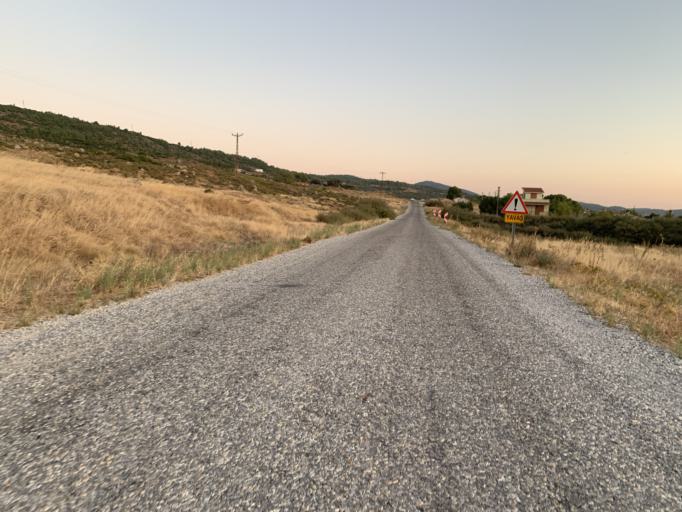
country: TR
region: Izmir
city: Uzunkuyu
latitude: 38.3265
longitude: 26.5837
